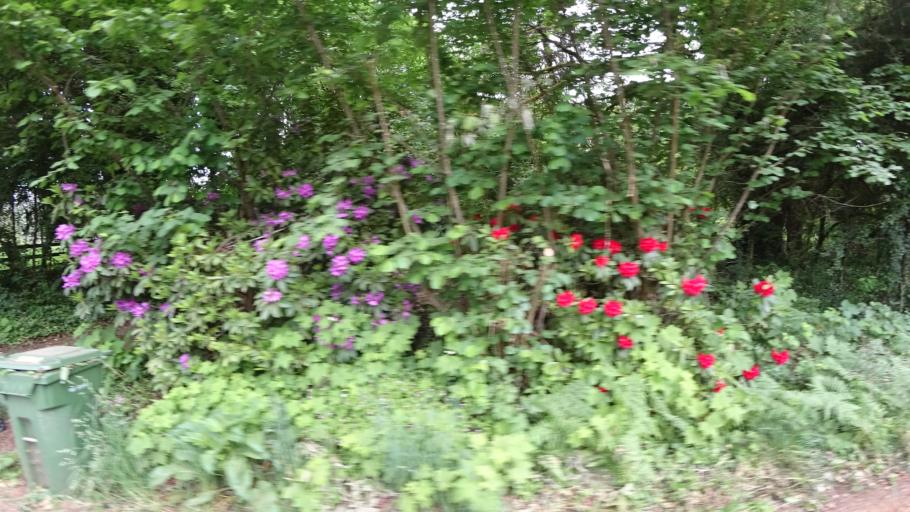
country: US
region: Oregon
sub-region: Clackamas County
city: Lake Oswego
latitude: 45.4257
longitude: -122.6839
